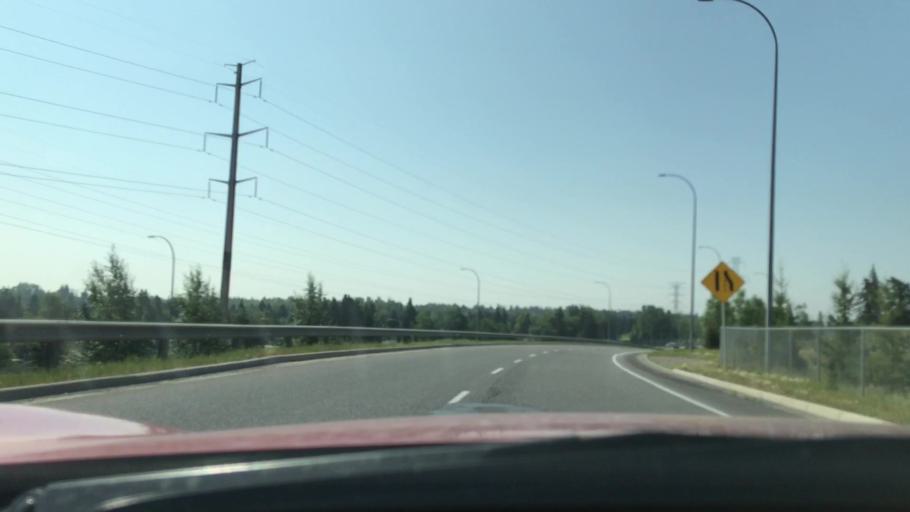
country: CA
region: Alberta
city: Calgary
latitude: 51.0389
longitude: -114.1656
